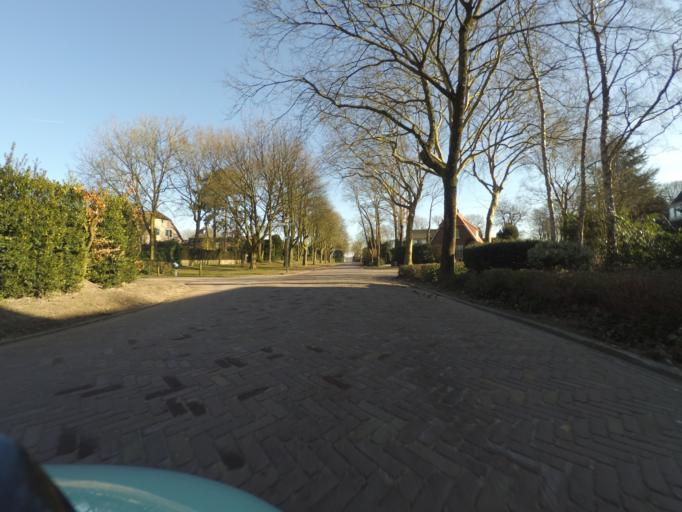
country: NL
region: North Holland
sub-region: Gemeente Blaricum
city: Blaricum
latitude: 52.2747
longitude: 5.2519
